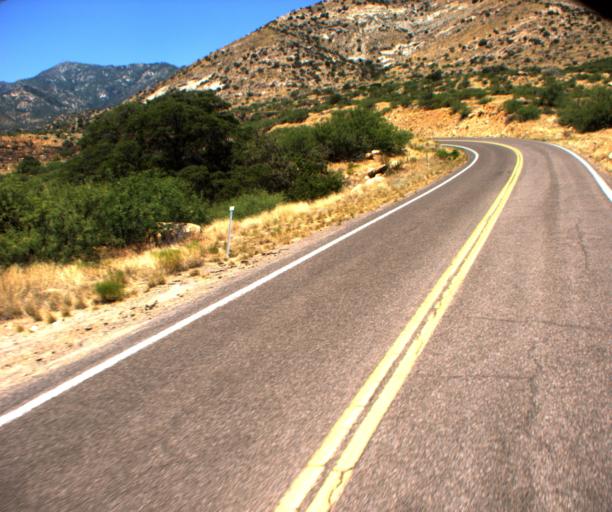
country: US
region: Arizona
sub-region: Graham County
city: Swift Trail Junction
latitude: 32.6789
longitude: -109.7742
